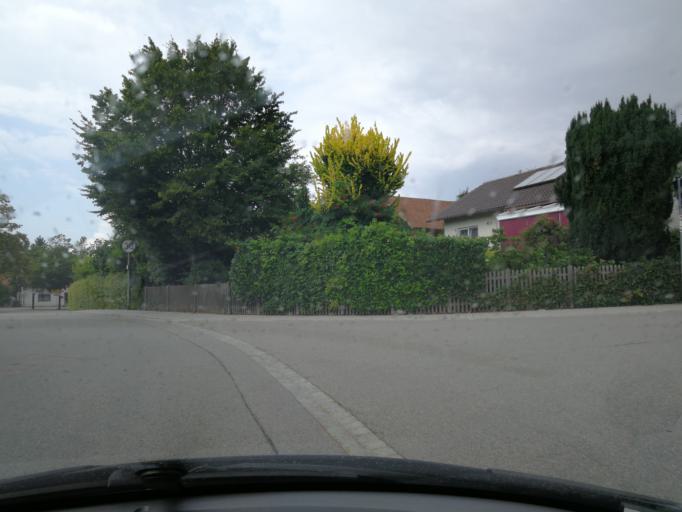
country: DE
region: Bavaria
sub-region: Upper Palatinate
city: Brennberg
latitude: 49.0700
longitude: 12.3977
